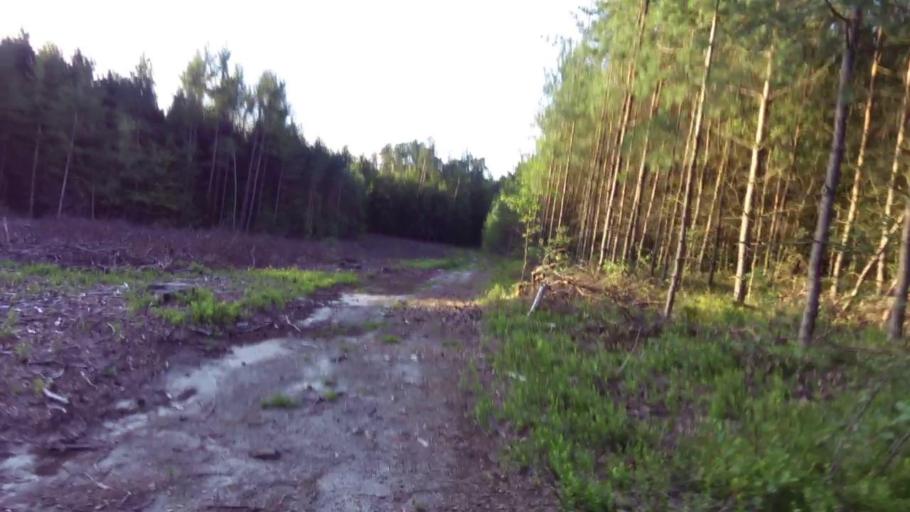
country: PL
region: West Pomeranian Voivodeship
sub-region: Powiat drawski
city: Zlocieniec
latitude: 53.5565
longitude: 16.0172
